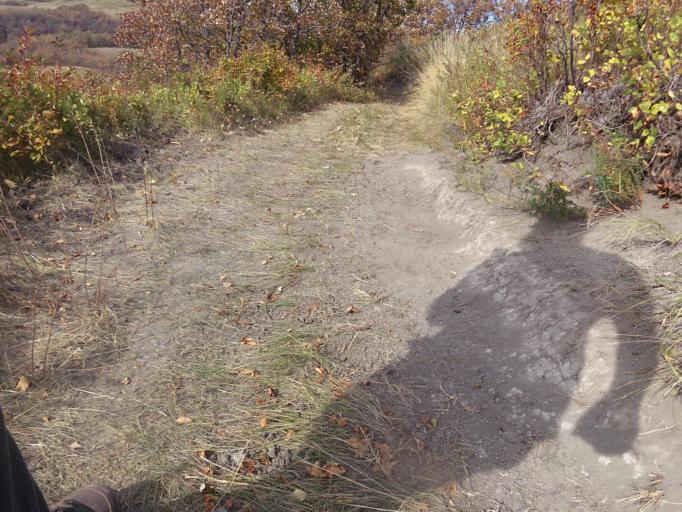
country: CA
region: Manitoba
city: Morden
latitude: 48.9479
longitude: -98.0684
